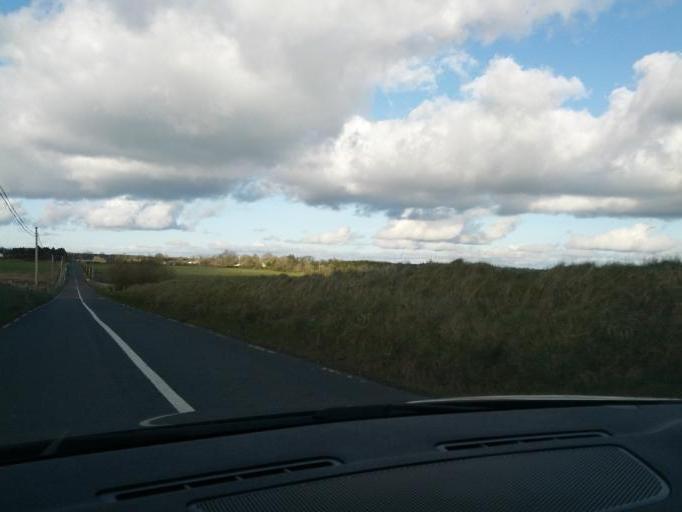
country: IE
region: Connaught
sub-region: Roscommon
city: Castlerea
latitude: 53.6449
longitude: -8.5259
